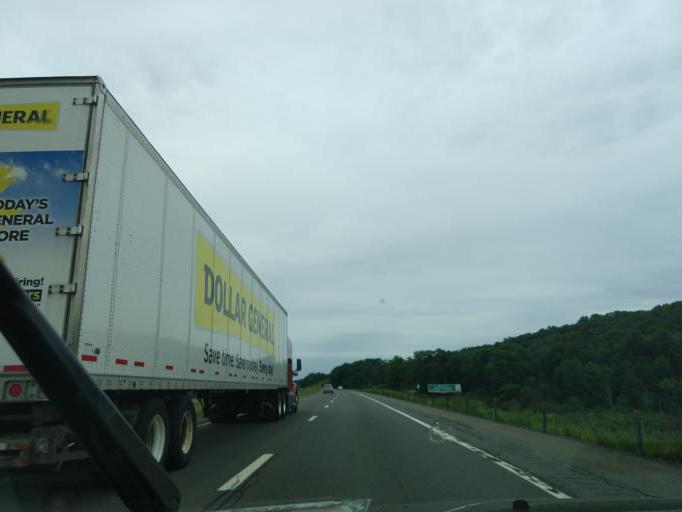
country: US
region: New York
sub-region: Broome County
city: Chenango Bridge
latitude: 42.2502
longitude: -75.9189
